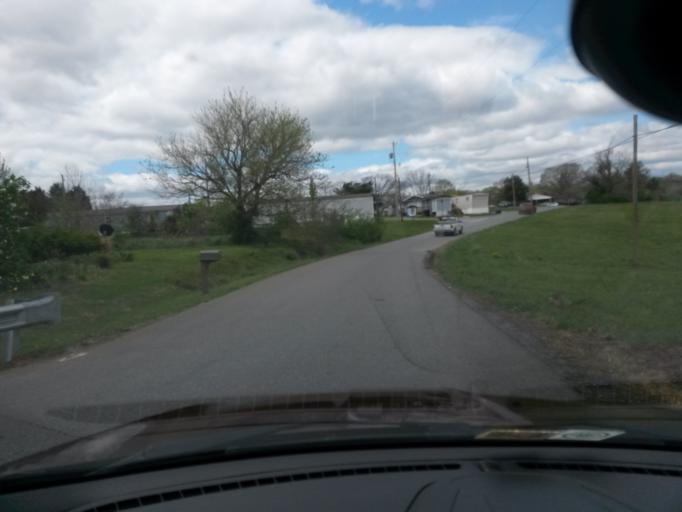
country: US
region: Virginia
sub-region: City of Lynchburg
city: West Lynchburg
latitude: 37.3977
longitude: -79.2120
